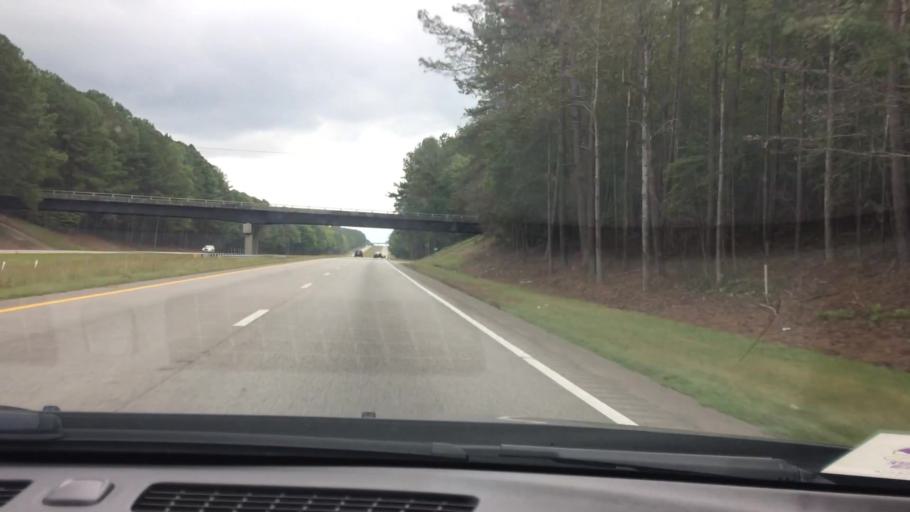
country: US
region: North Carolina
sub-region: Wake County
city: Zebulon
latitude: 35.8145
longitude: -78.2417
